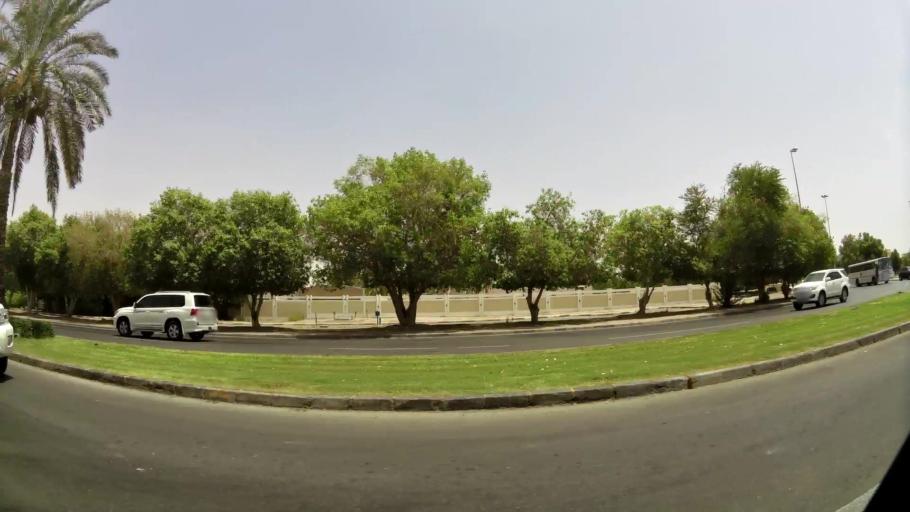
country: AE
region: Abu Dhabi
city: Al Ain
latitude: 24.2050
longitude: 55.7462
